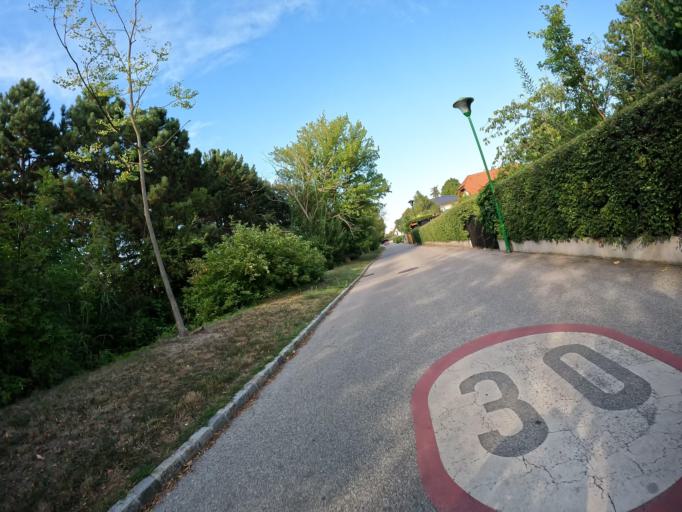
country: AT
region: Lower Austria
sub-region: Politischer Bezirk Modling
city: Guntramsdorf
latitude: 48.0429
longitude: 16.3101
